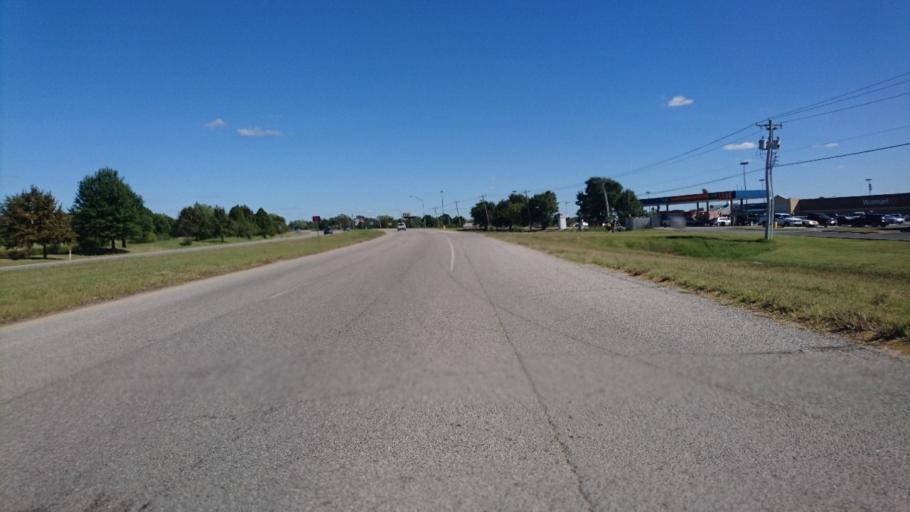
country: US
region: Oklahoma
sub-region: Creek County
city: Sapulpa
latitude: 35.9886
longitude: -96.1366
